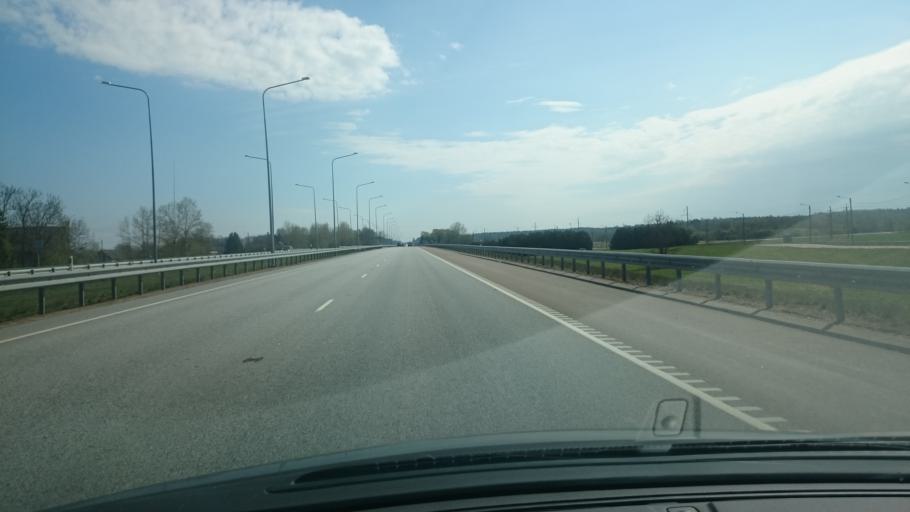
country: EE
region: Harju
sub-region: Kuusalu vald
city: Kuusalu
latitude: 59.4449
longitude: 25.3722
